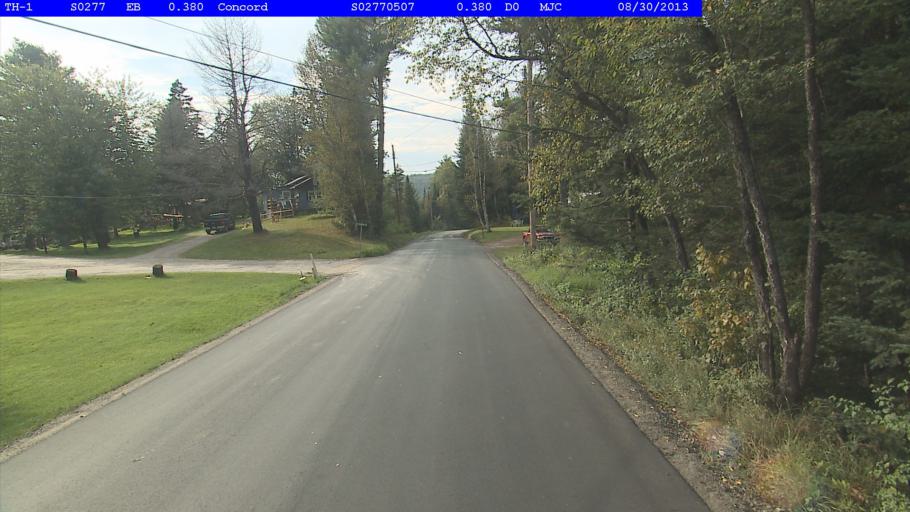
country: US
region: Vermont
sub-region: Caledonia County
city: Lyndonville
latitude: 44.4700
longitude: -71.8596
